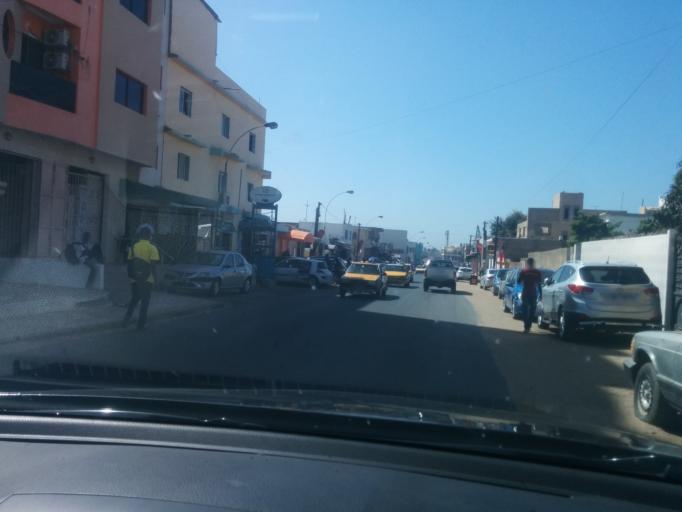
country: SN
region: Dakar
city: Grand Dakar
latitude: 14.7456
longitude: -17.4433
